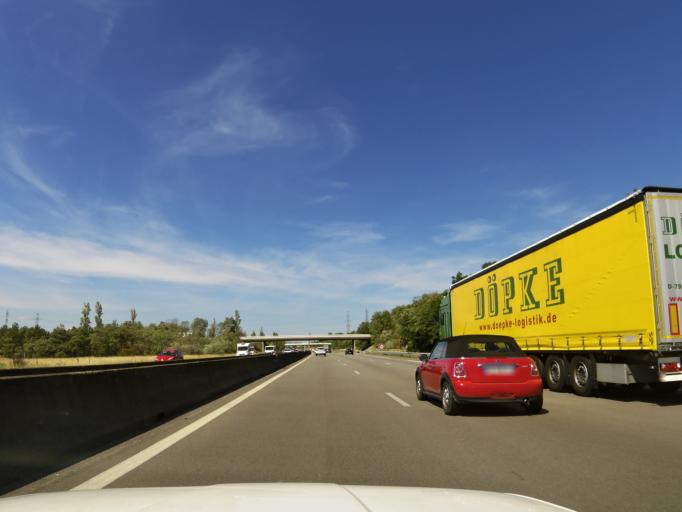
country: FR
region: Rhone-Alpes
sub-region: Departement de l'Isere
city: Chanas
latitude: 45.3220
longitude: 4.8122
